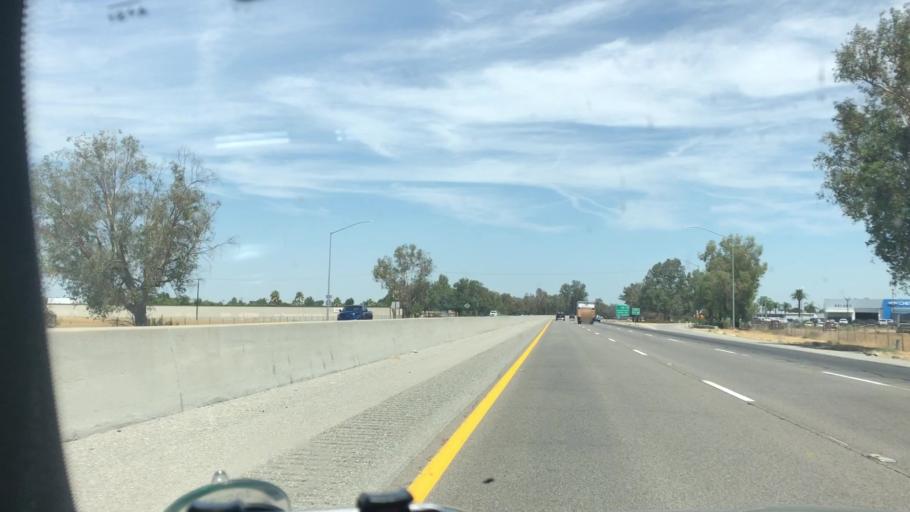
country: US
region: California
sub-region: Kern County
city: Delano
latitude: 35.7542
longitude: -119.2469
